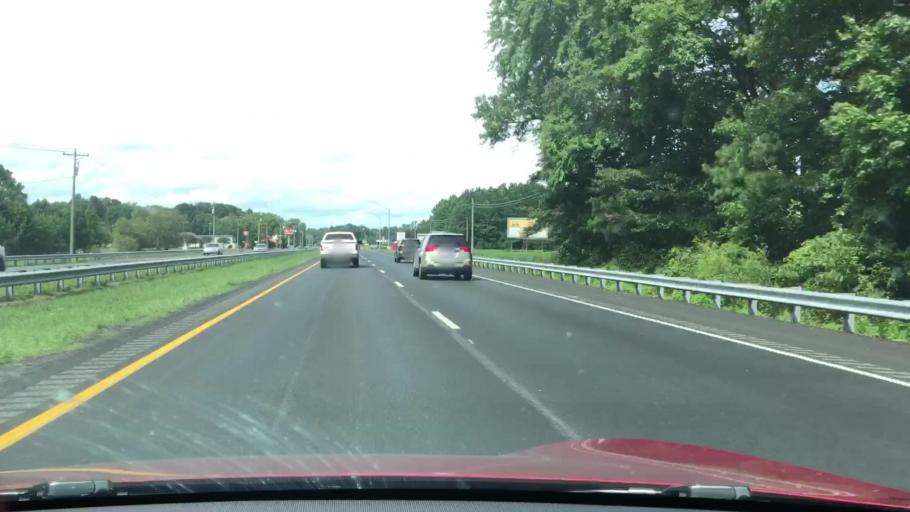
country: US
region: Maryland
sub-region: Worcester County
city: Pocomoke City
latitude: 38.0240
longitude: -75.5423
